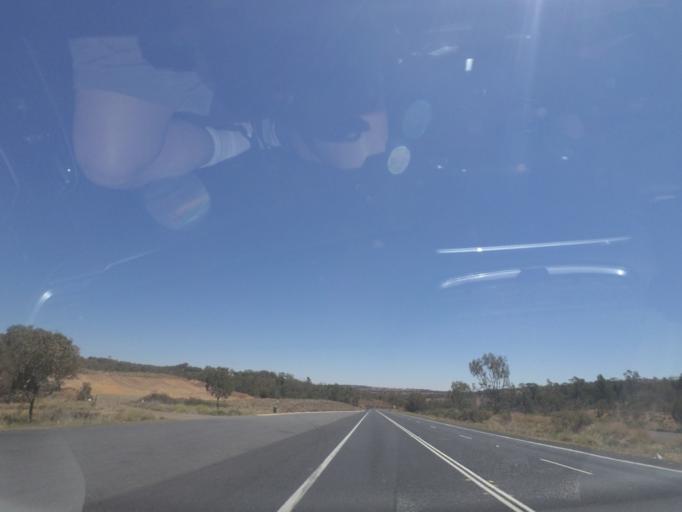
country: AU
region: New South Wales
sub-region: Warrumbungle Shire
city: Coonabarabran
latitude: -31.4271
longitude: 149.0791
